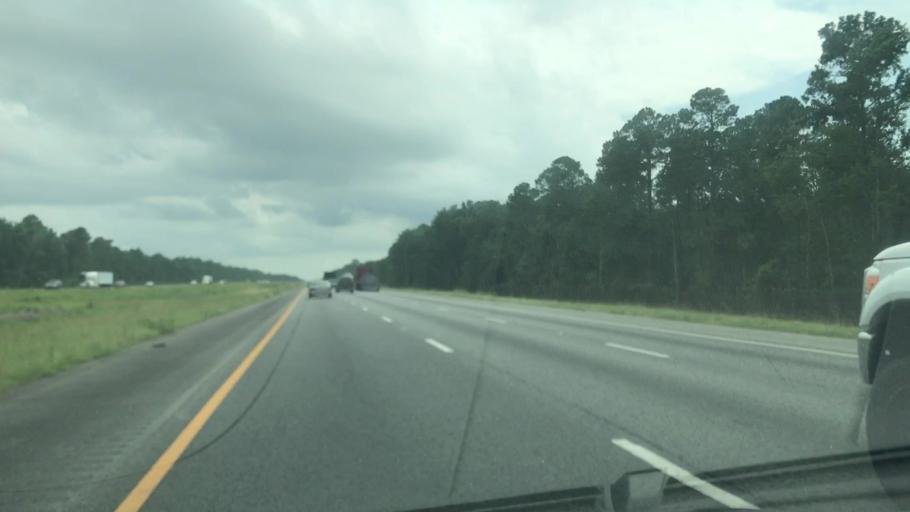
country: US
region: Georgia
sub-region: Glynn County
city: Brunswick
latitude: 31.0807
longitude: -81.6157
